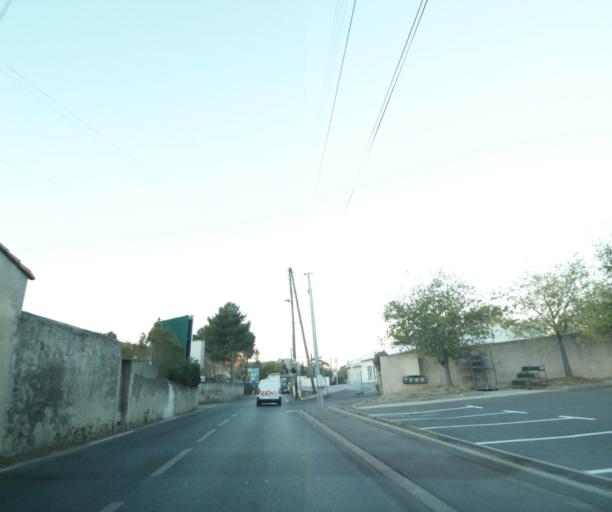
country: FR
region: Provence-Alpes-Cote d'Azur
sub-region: Departement des Bouches-du-Rhone
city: La Penne-sur-Huveaune
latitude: 43.2980
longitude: 5.4980
